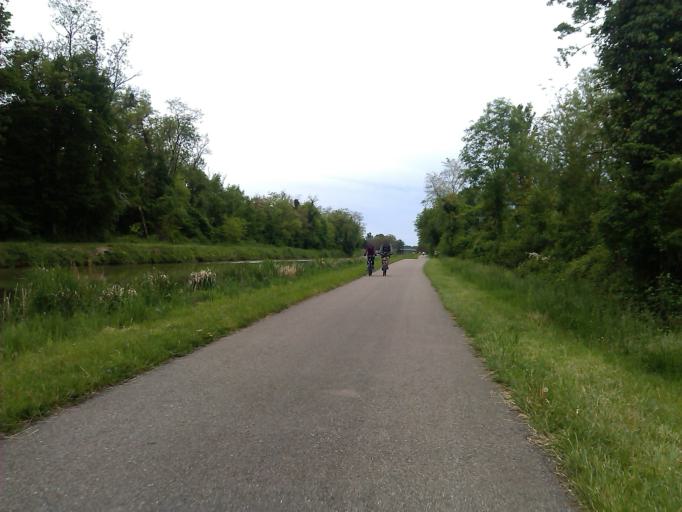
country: FR
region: Franche-Comte
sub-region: Departement du Jura
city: Choisey
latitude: 47.0663
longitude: 5.4651
